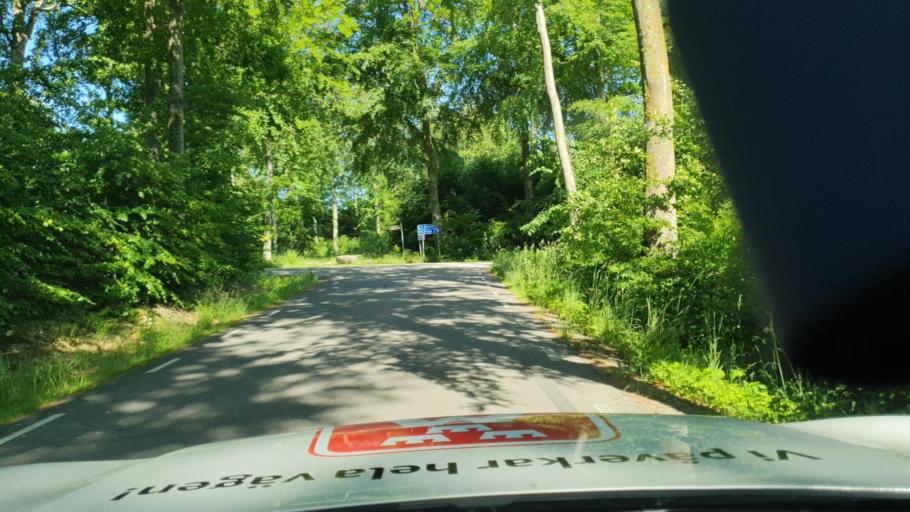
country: SE
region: Skane
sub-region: Sjobo Kommun
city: Sjoebo
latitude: 55.6505
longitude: 13.7582
